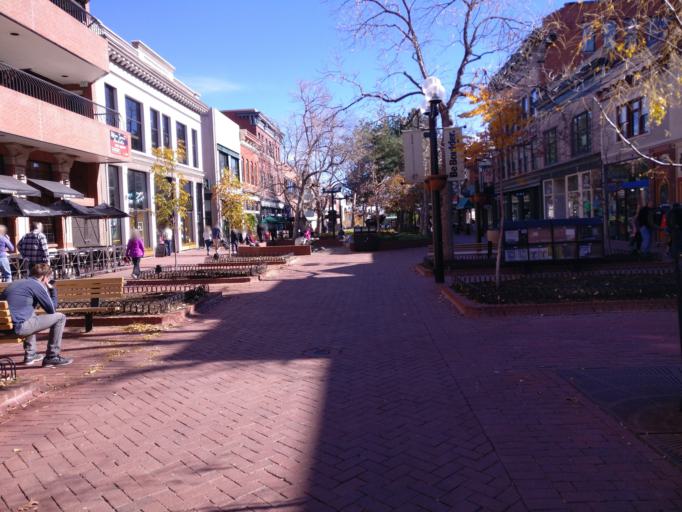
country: US
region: Colorado
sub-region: Boulder County
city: Boulder
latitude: 40.0184
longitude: -105.2771
